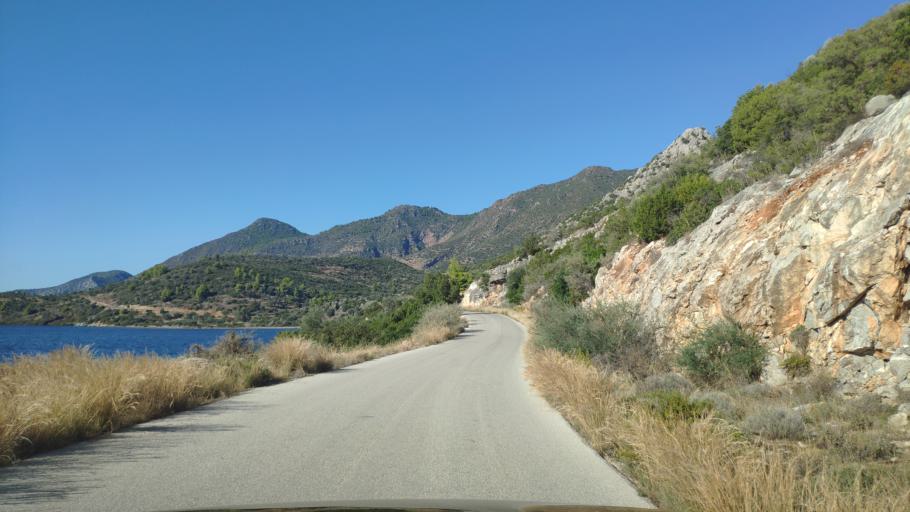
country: GR
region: Attica
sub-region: Nomos Piraios
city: Galatas
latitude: 37.5723
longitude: 23.3599
